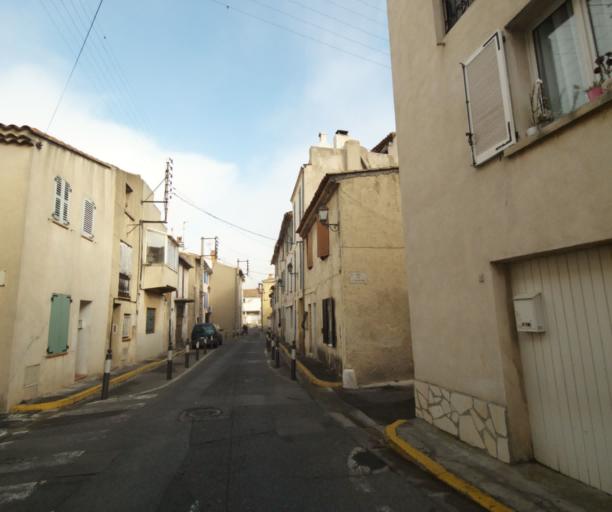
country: FR
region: Provence-Alpes-Cote d'Azur
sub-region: Departement des Bouches-du-Rhone
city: Marignane
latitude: 43.4156
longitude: 5.2134
